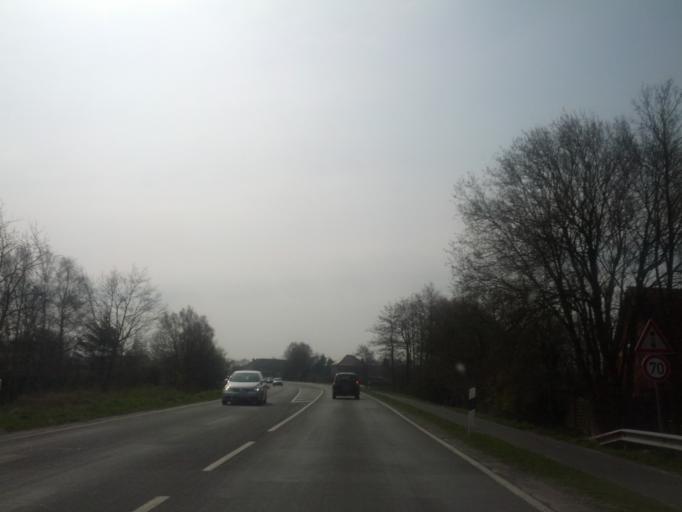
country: DE
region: Lower Saxony
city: Osteel
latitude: 53.5490
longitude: 7.2550
